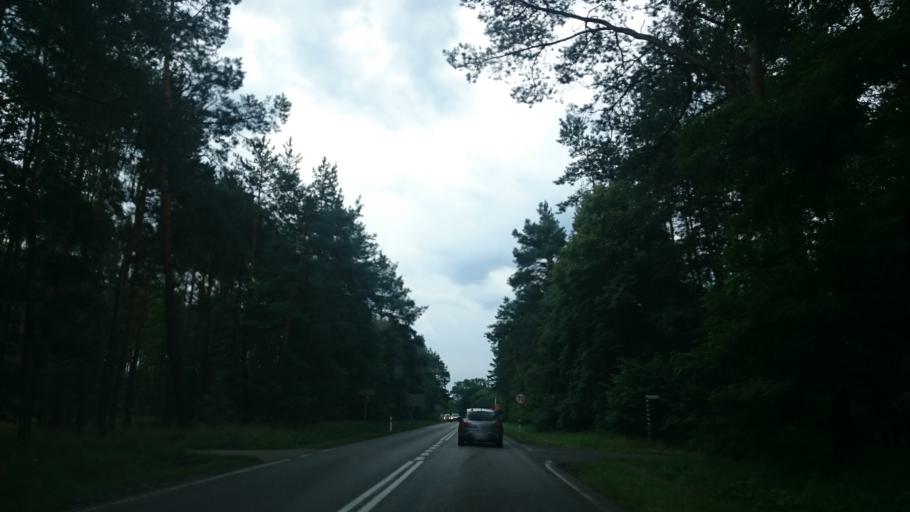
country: PL
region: Kujawsko-Pomorskie
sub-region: Powiat tucholski
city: Cekcyn
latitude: 53.5213
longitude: 17.9510
